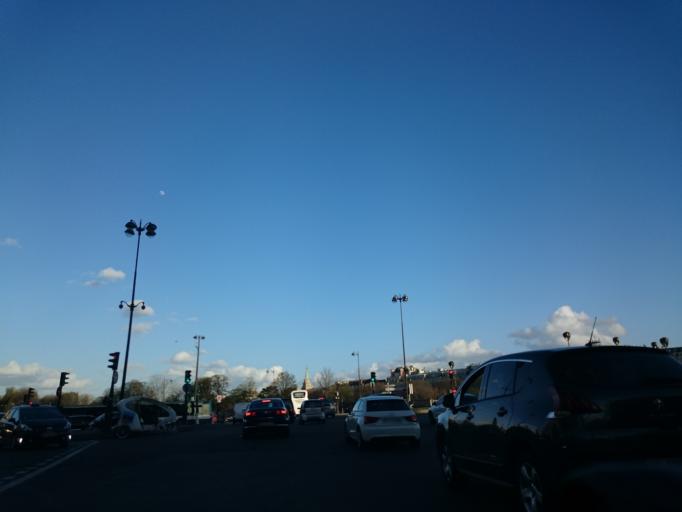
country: FR
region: Ile-de-France
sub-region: Departement des Hauts-de-Seine
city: Levallois-Perret
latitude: 48.8646
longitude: 2.3011
